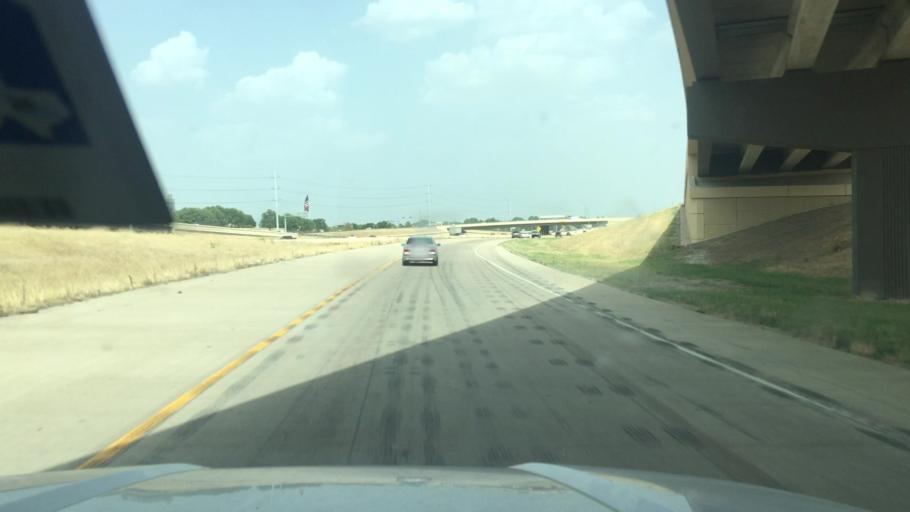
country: US
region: Texas
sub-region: Denton County
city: Roanoke
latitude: 32.9980
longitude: -97.2127
